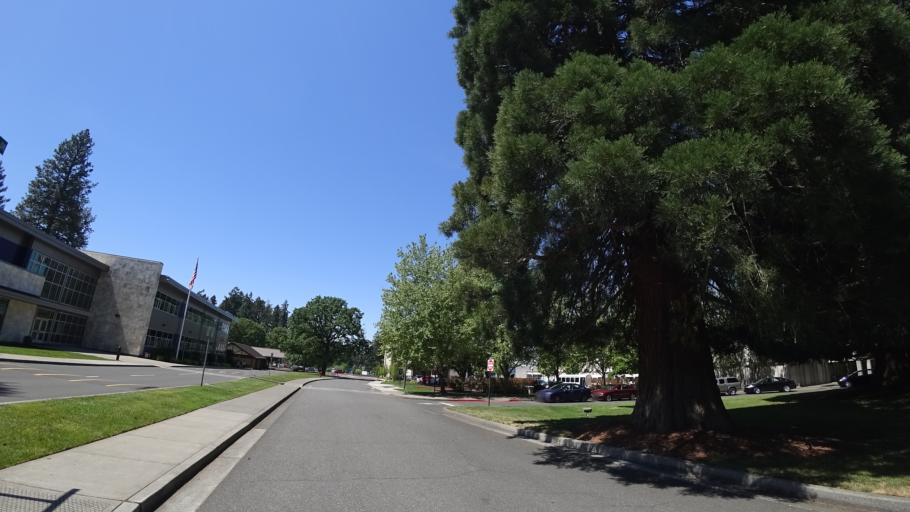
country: US
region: Oregon
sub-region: Washington County
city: Beaverton
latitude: 45.4879
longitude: -122.8290
